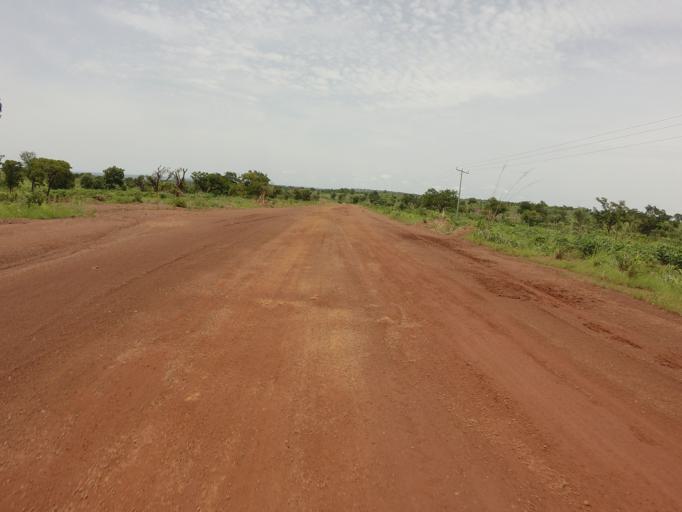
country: GH
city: Kpandae
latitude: 8.7453
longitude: 0.0770
